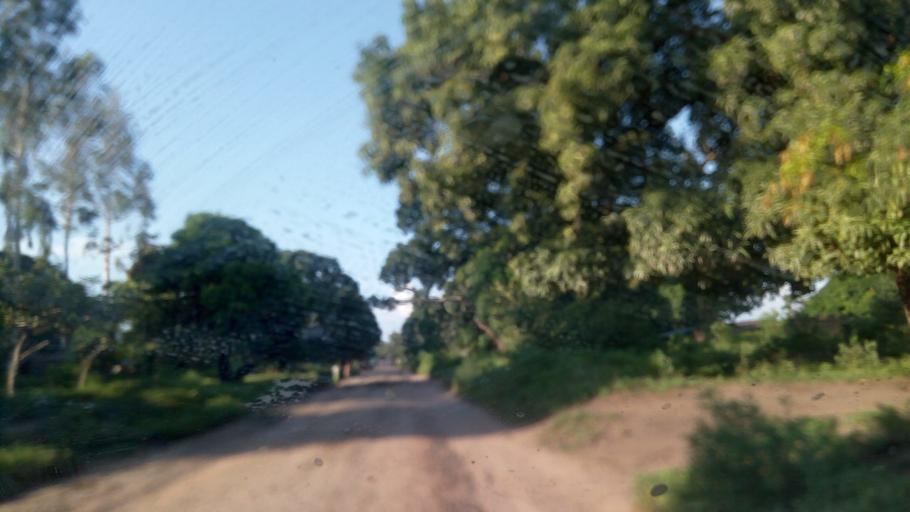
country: BI
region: Bururi
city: Rumonge
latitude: -4.1954
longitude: 29.0496
